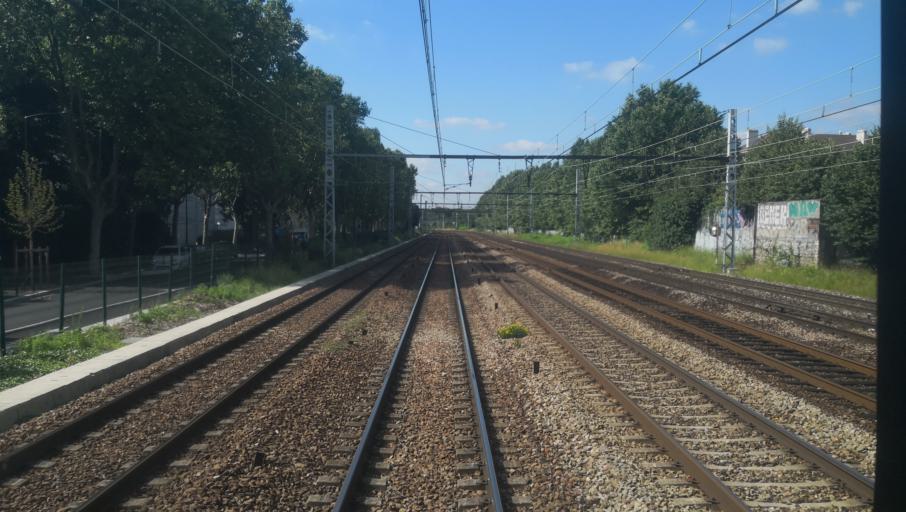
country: FR
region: Ile-de-France
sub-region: Departement du Val-de-Marne
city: Alfortville
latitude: 48.8047
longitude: 2.4254
